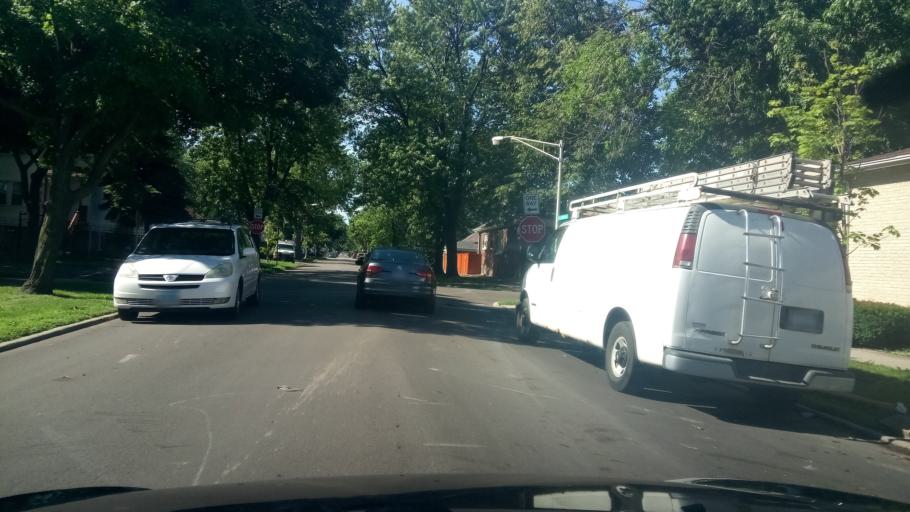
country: US
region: Illinois
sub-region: Cook County
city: Hometown
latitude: 41.7780
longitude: -87.7154
